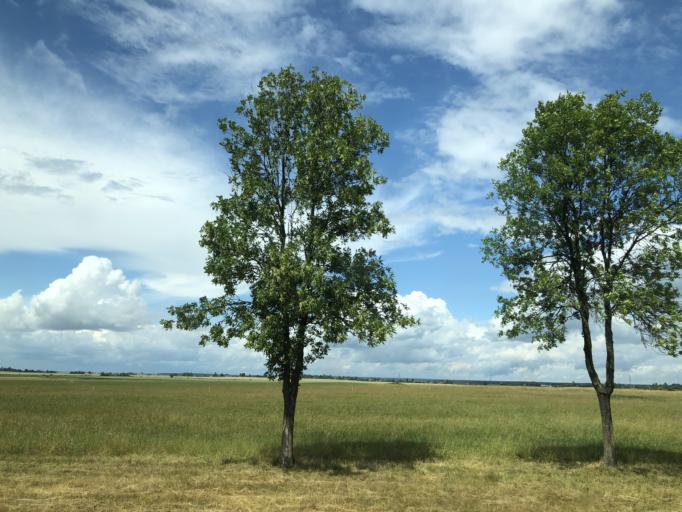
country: BY
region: Minsk
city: Tsimkavichy
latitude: 53.2517
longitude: 26.9092
